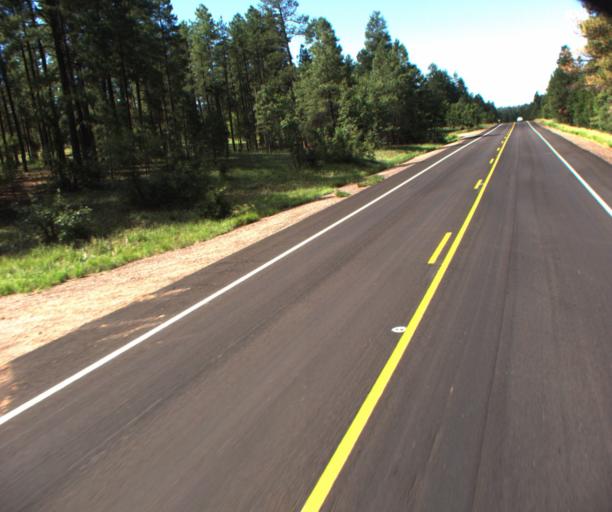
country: US
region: Arizona
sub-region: Navajo County
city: Show Low
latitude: 34.1986
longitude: -110.0859
